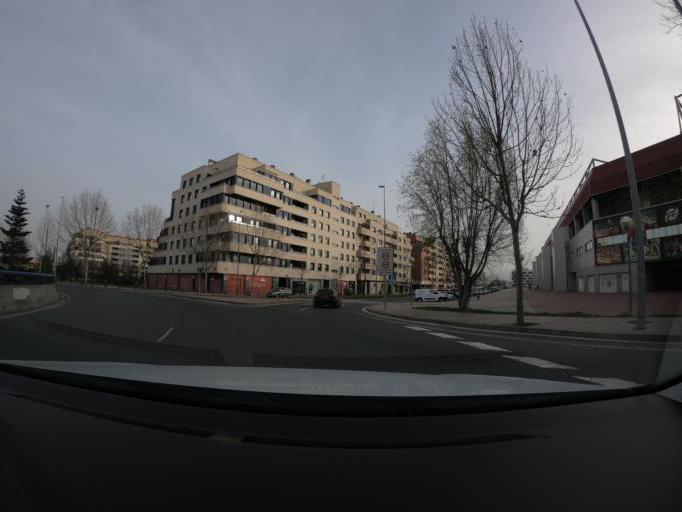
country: ES
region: La Rioja
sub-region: Provincia de La Rioja
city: Logrono
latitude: 42.4539
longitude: -2.4521
